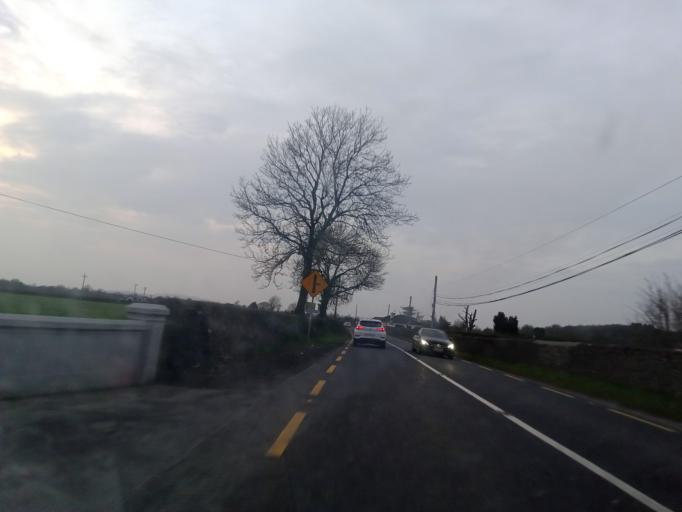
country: IE
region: Leinster
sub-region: Kilkenny
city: Kilkenny
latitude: 52.7192
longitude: -7.2948
